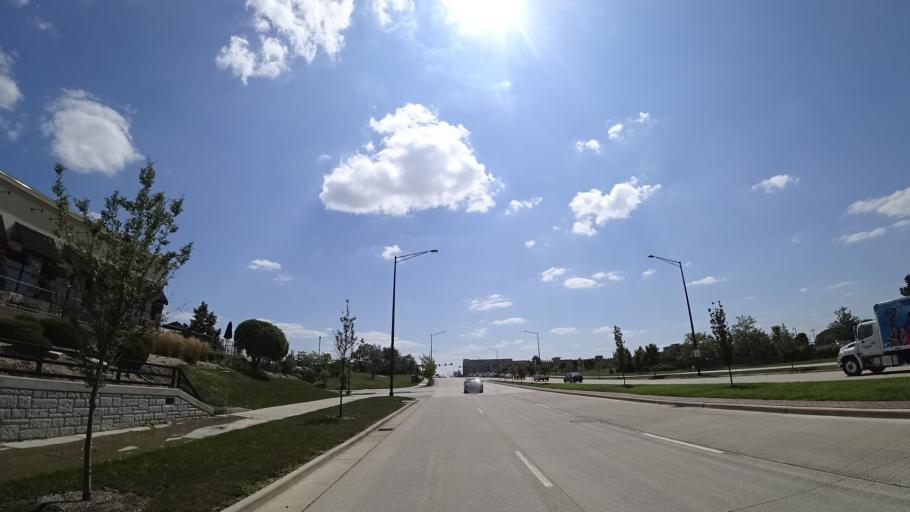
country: US
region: Illinois
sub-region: Cook County
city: Orland Park
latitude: 41.6345
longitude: -87.8538
